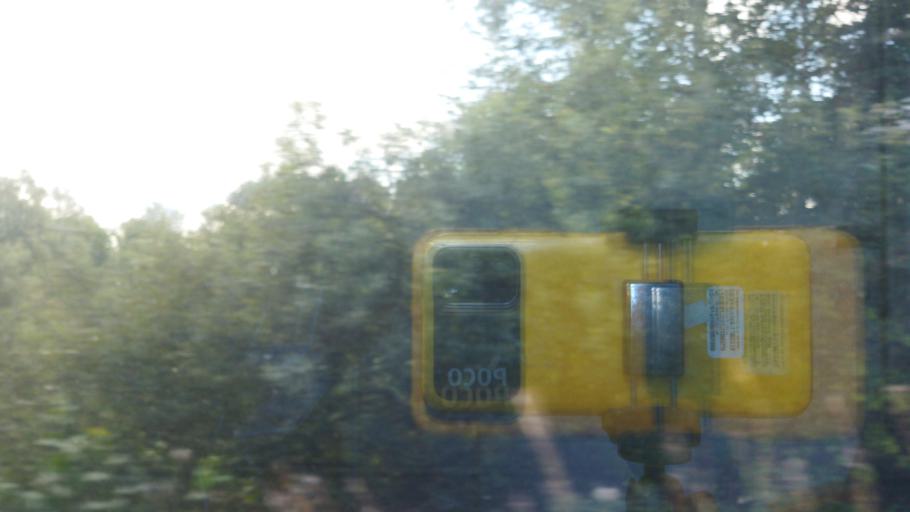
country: DE
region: Lower Saxony
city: Emden
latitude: 53.3398
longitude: 7.2771
